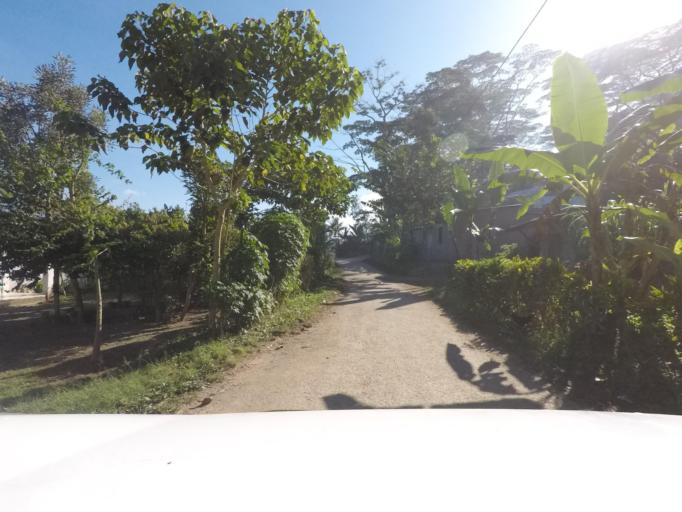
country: TL
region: Ermera
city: Gleno
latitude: -8.7321
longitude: 125.4321
